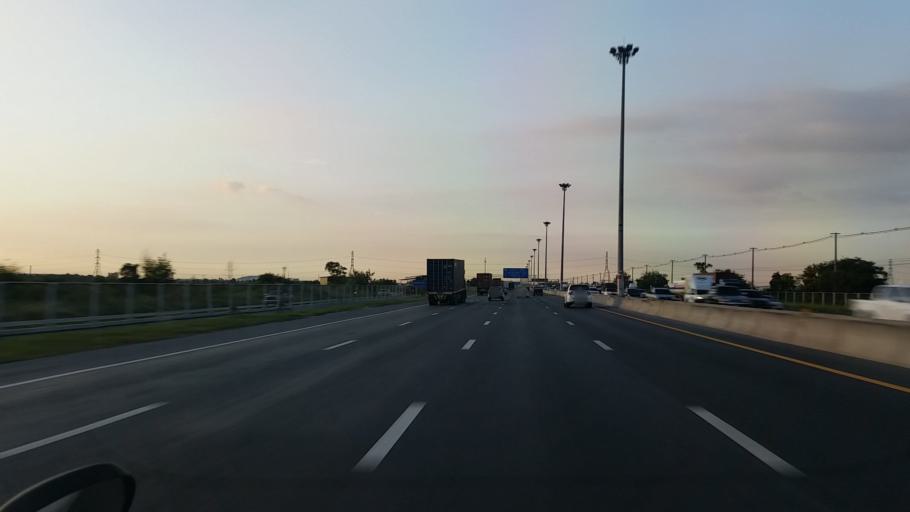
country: TH
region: Phra Nakhon Si Ayutthaya
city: Wang Noi
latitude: 14.1630
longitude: 100.6514
